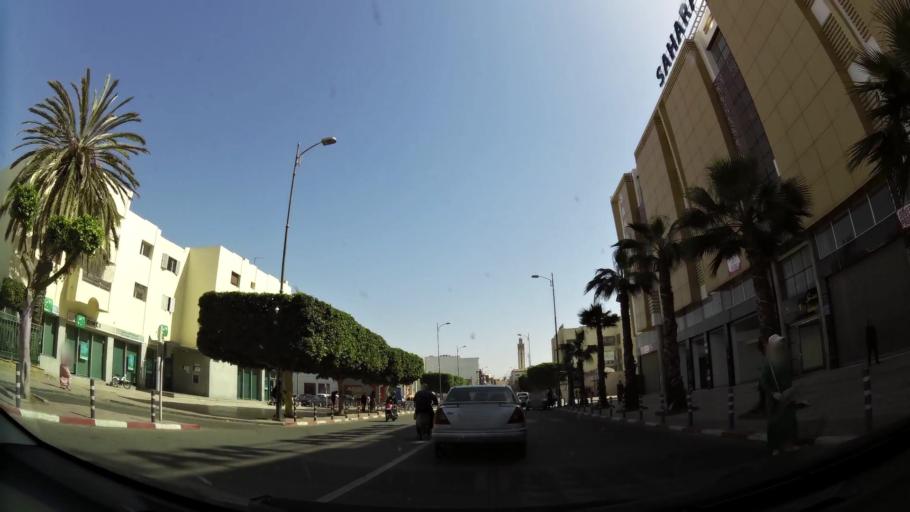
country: MA
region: Souss-Massa-Draa
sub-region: Inezgane-Ait Mellou
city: Inezgane
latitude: 30.3594
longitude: -9.5335
